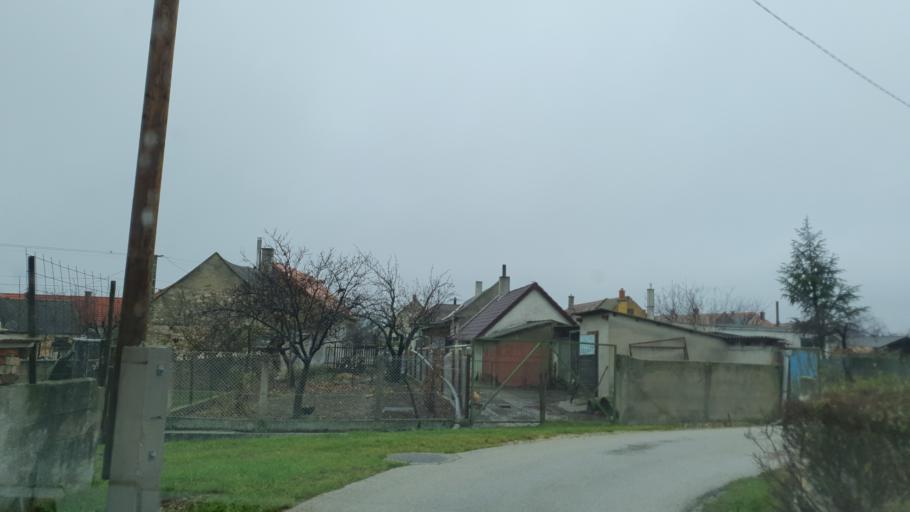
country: HU
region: Veszprem
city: Hajmasker
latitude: 47.1446
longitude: 17.9554
